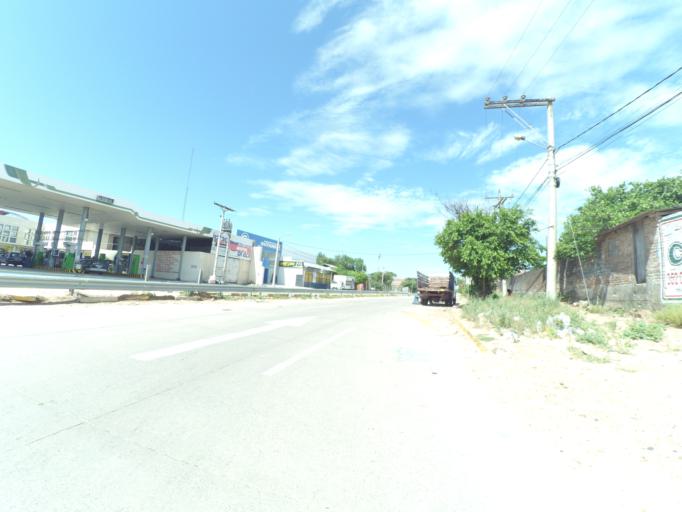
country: BO
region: Santa Cruz
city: Santa Cruz de la Sierra
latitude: -17.8010
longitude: -63.2159
